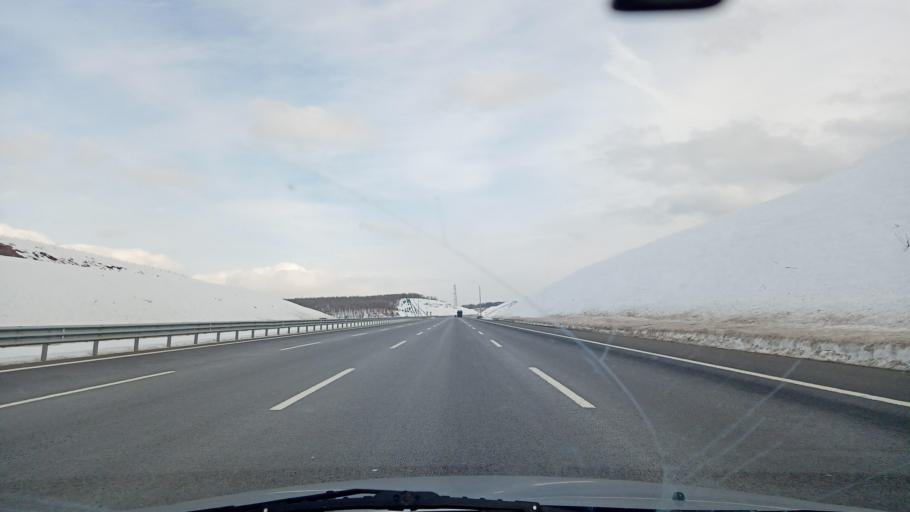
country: TR
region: Kocaeli
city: Hereke
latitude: 40.8967
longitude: 29.6299
